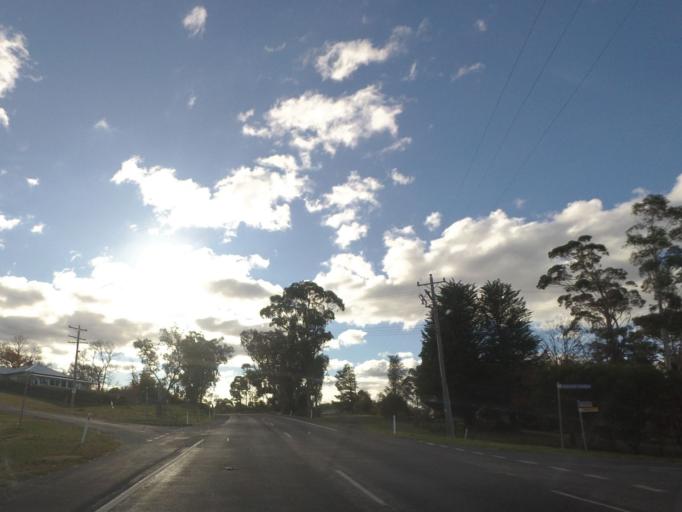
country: AU
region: Victoria
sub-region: Mount Alexander
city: Castlemaine
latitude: -37.1368
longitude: 144.3469
